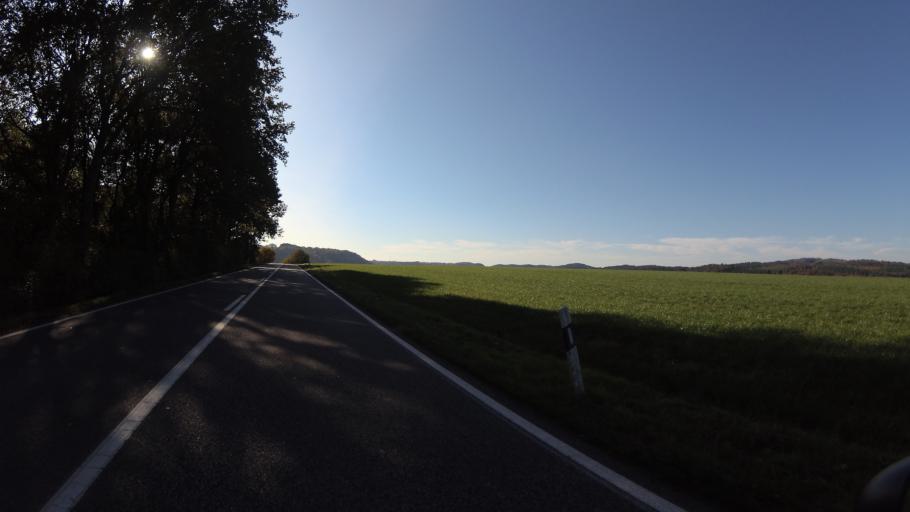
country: DE
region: Saarland
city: Losheim
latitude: 49.4859
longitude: 6.7142
